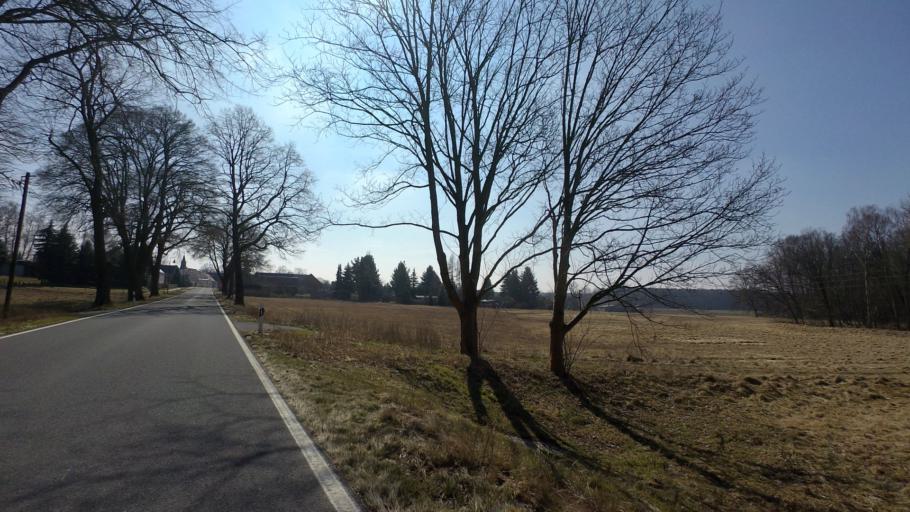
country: DE
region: Saxony-Anhalt
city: Nudersdorf
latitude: 52.0234
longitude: 12.5312
